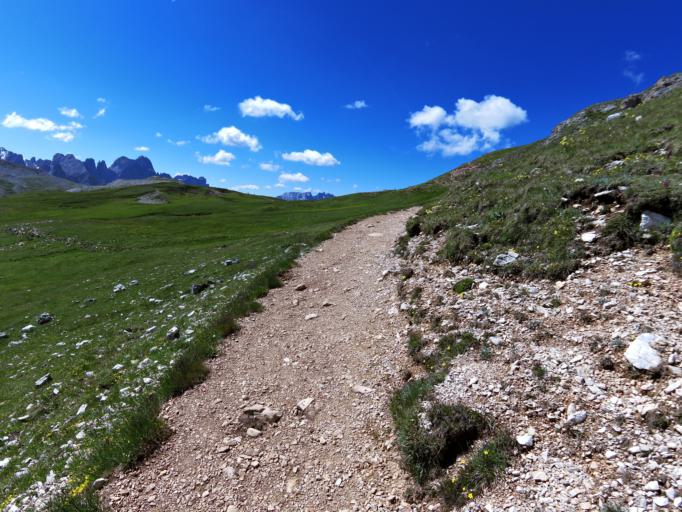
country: IT
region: Trentino-Alto Adige
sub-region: Bolzano
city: Siusi
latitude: 46.5110
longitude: 11.5813
